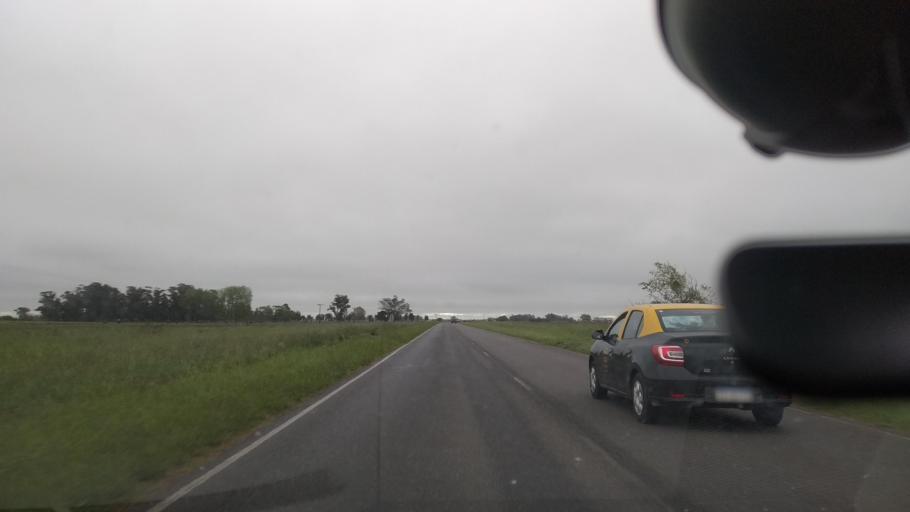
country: AR
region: Buenos Aires
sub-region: Partido de Magdalena
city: Magdalena
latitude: -35.2265
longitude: -57.7245
